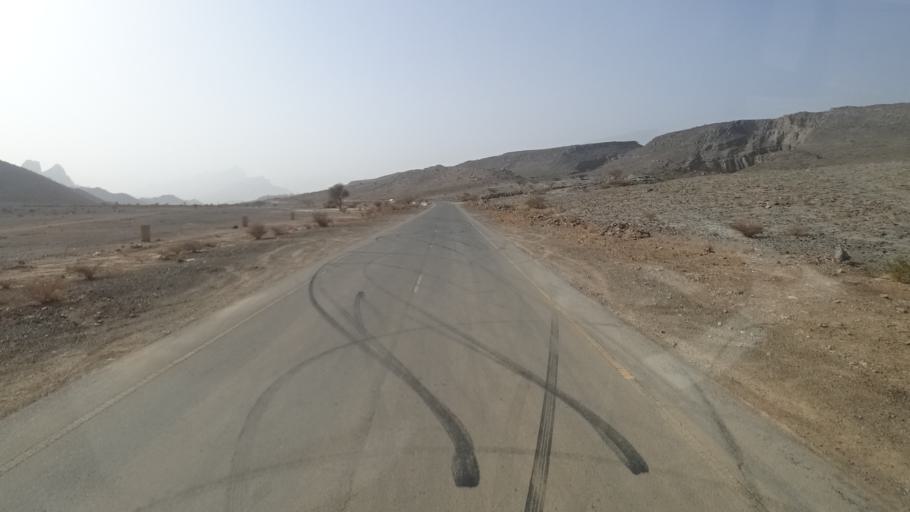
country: OM
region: Muhafazat ad Dakhiliyah
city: Bahla'
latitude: 23.0758
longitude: 57.3570
